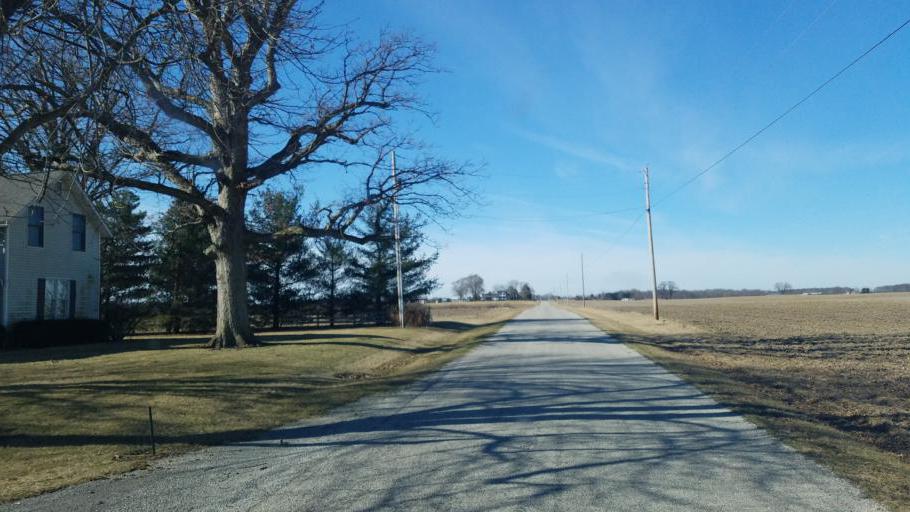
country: US
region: Ohio
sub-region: Union County
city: Richwood
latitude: 40.5249
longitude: -83.3715
